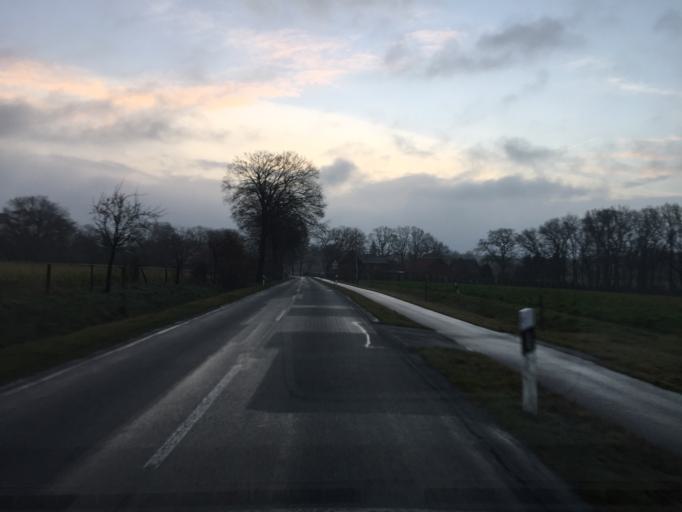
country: DE
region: Lower Saxony
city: Pennigsehl
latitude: 52.6295
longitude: 9.0301
